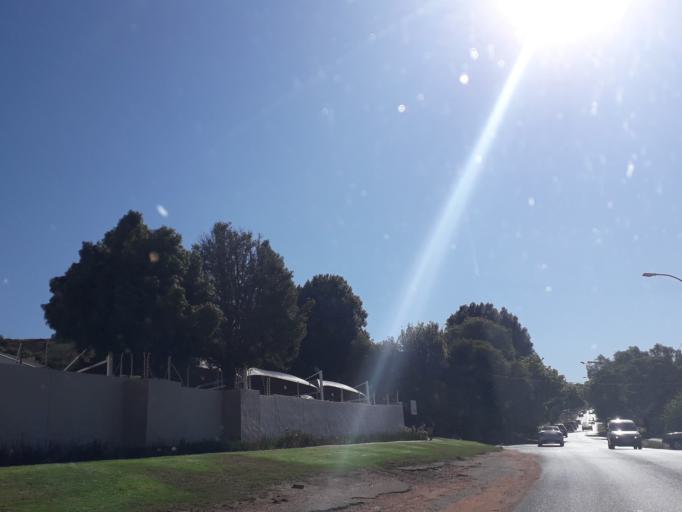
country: ZA
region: Gauteng
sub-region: City of Johannesburg Metropolitan Municipality
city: Roodepoort
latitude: -26.1510
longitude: 27.9437
